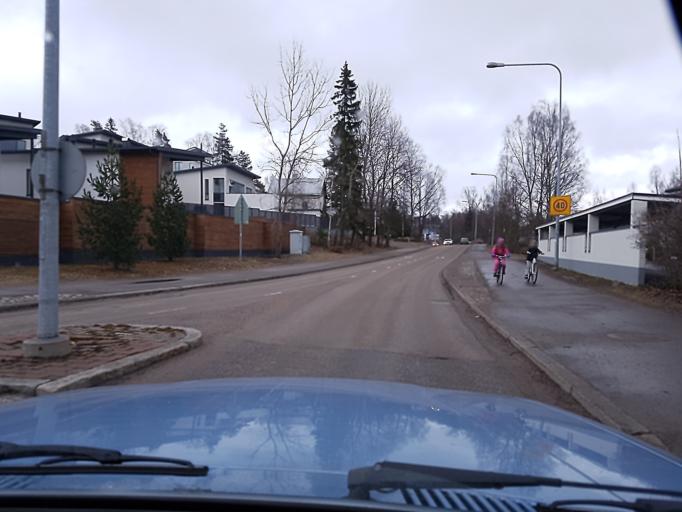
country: FI
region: Uusimaa
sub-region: Helsinki
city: Kilo
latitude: 60.1909
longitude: 24.7766
